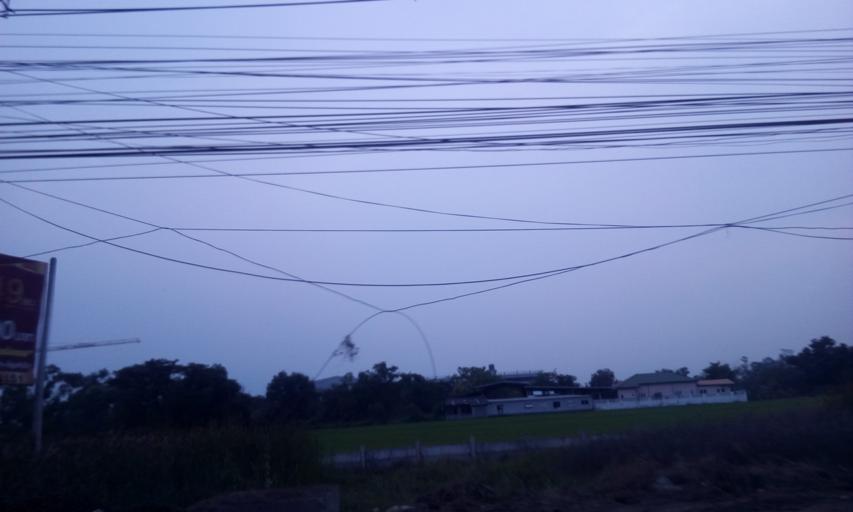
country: TH
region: Chachoengsao
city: Bang Nam Priao
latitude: 13.7753
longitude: 100.9695
